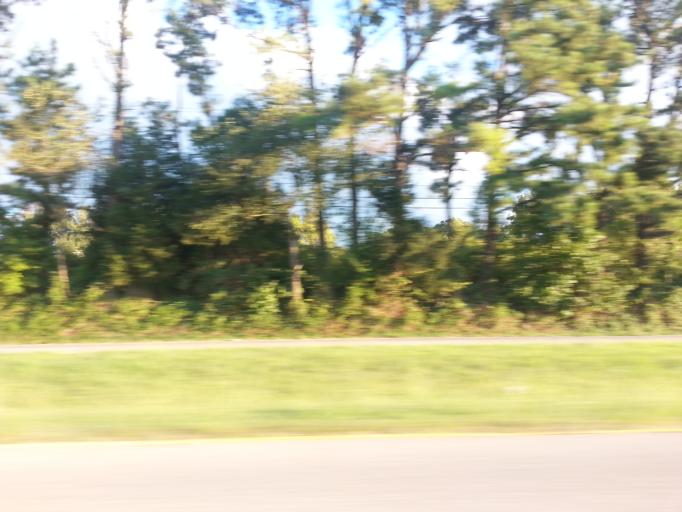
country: US
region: Tennessee
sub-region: Jefferson County
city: New Market
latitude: 36.0909
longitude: -83.5864
